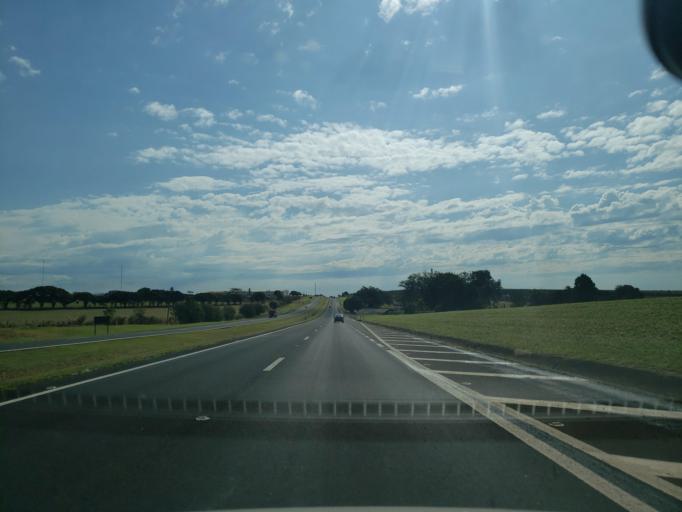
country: BR
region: Sao Paulo
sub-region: Pirajui
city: Pirajui
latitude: -22.0109
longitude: -49.4210
